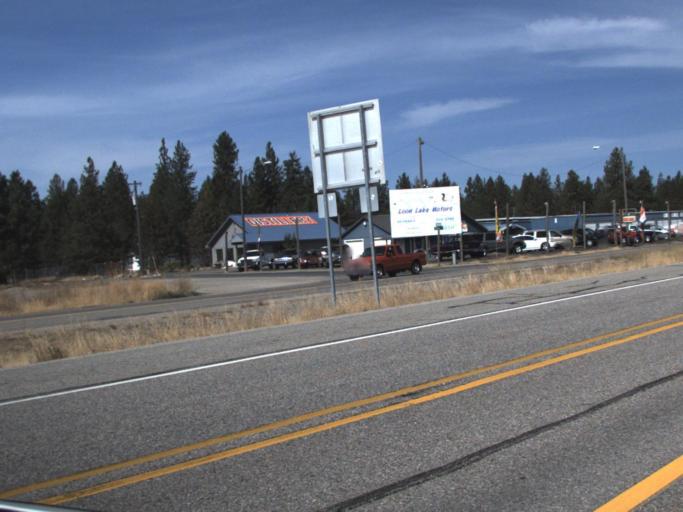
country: US
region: Washington
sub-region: Spokane County
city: Deer Park
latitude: 48.0611
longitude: -117.6211
